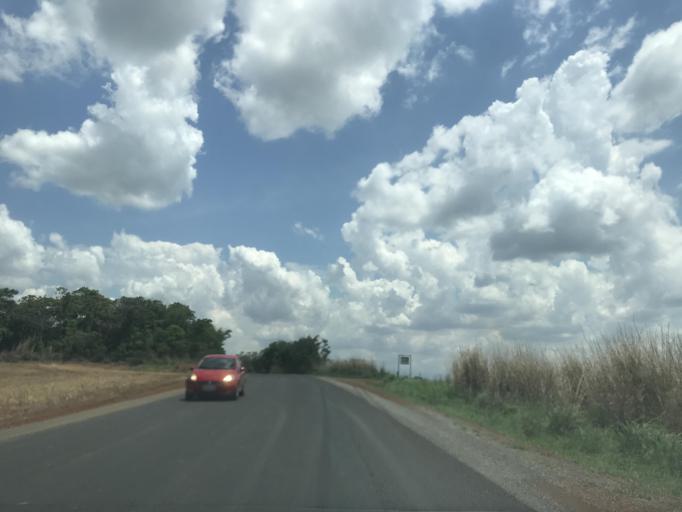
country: BR
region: Goias
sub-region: Piracanjuba
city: Piracanjuba
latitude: -17.3275
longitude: -48.8011
